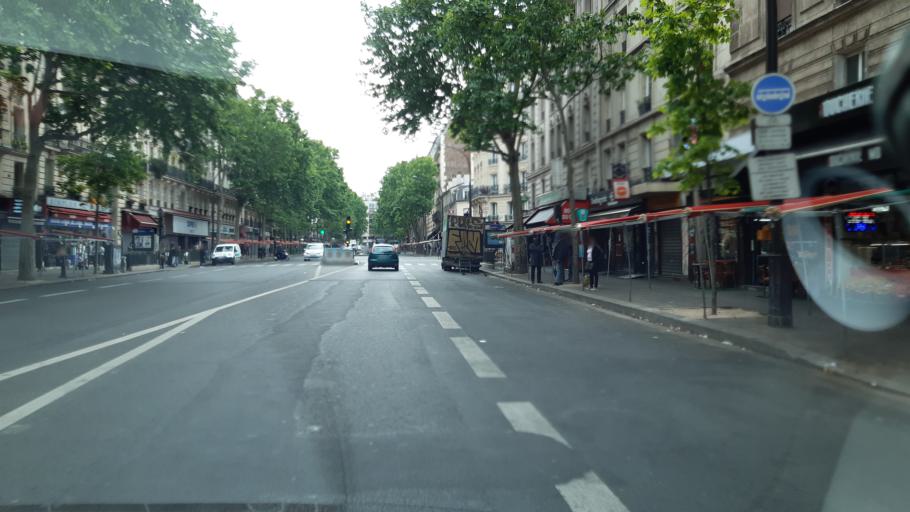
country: FR
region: Ile-de-France
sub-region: Paris
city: Saint-Ouen
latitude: 48.8944
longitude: 2.3473
